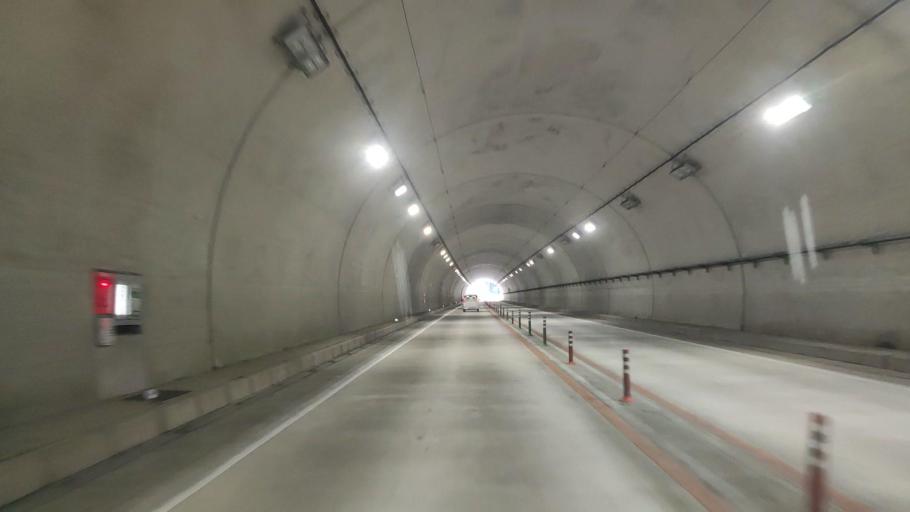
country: JP
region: Wakayama
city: Shingu
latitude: 33.6306
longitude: 135.9231
